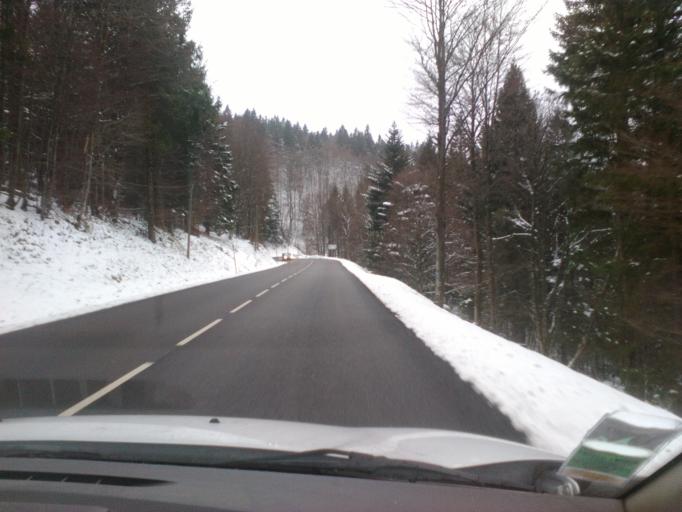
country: FR
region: Alsace
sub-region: Departement du Haut-Rhin
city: Metzeral
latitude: 48.0588
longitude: 7.0117
